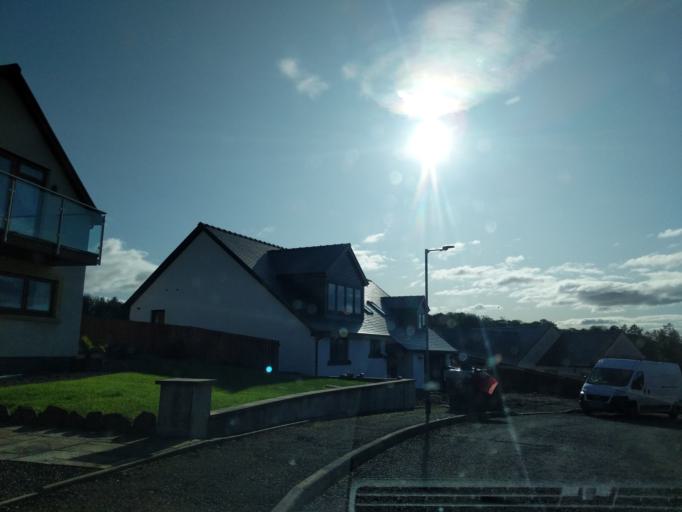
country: GB
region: Scotland
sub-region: Dumfries and Galloway
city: Kirkcudbright
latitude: 54.8289
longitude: -4.0502
